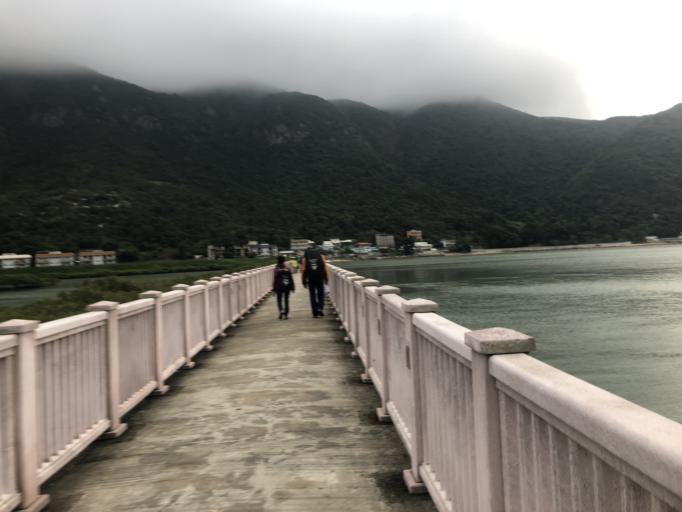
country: HK
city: Tai O
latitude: 22.2498
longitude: 113.8609
